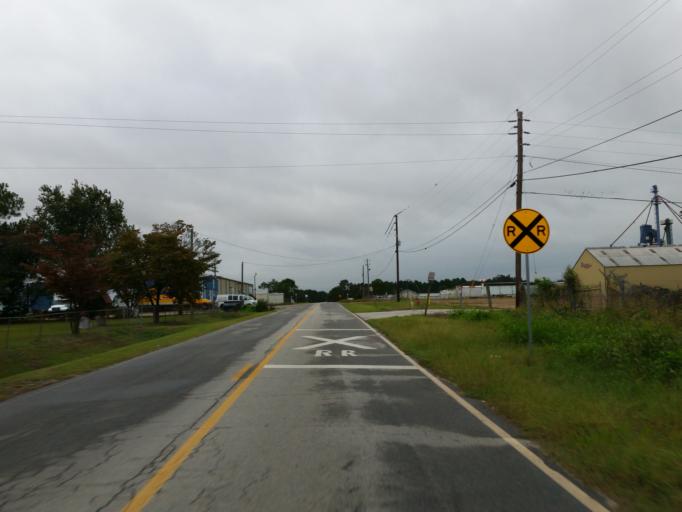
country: US
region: Georgia
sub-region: Turner County
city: Ashburn
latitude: 31.6803
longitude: -83.6376
